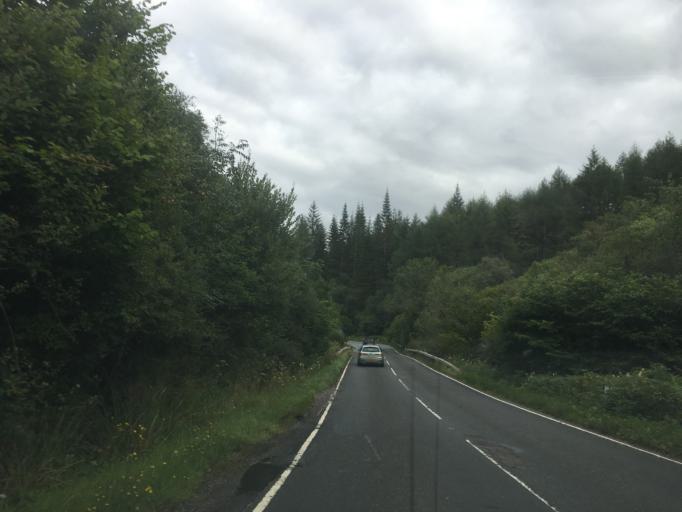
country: GB
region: Scotland
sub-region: Argyll and Bute
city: Oban
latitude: 56.3131
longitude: -5.4797
